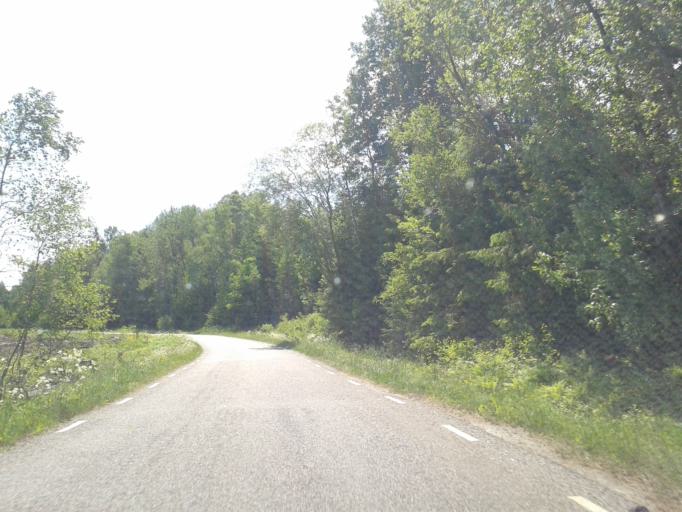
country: SE
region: Vaestra Goetaland
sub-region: Kungalvs Kommun
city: Diserod
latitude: 57.9894
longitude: 11.9569
